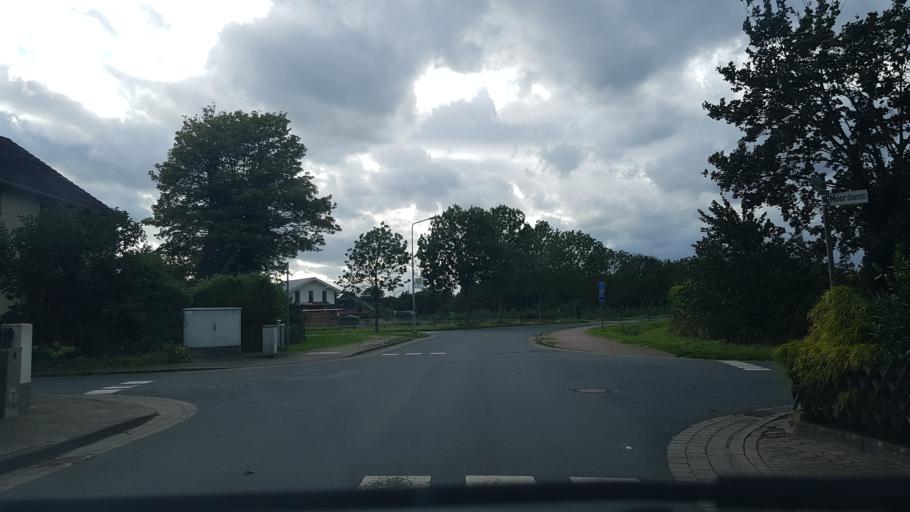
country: DE
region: Lower Saxony
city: Oyten
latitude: 53.0326
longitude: 8.9747
